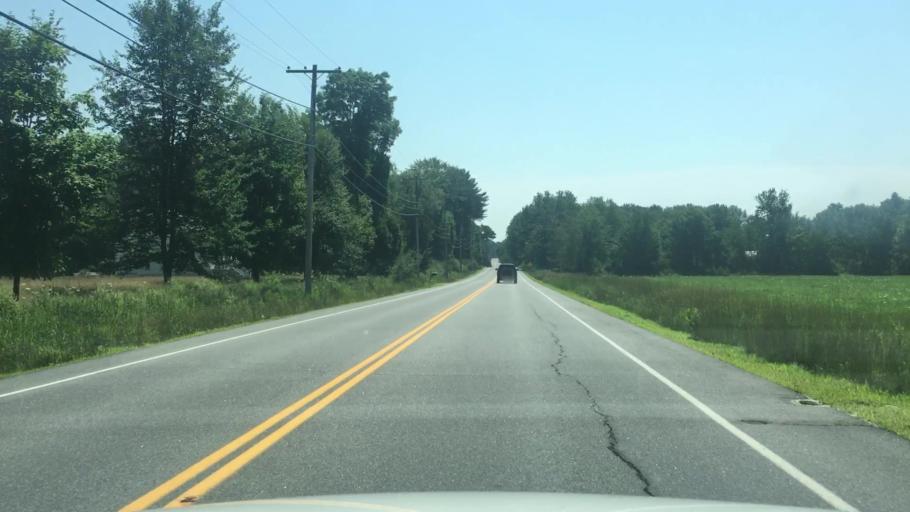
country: US
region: Maine
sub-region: Cumberland County
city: Cumberland Center
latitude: 43.8083
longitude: -70.2821
